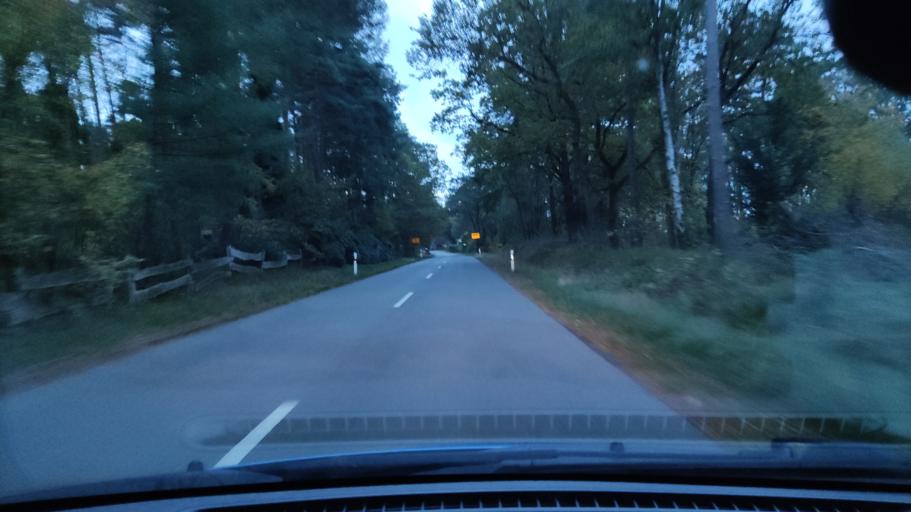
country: DE
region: Lower Saxony
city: Prezelle
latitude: 52.9670
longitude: 11.3997
